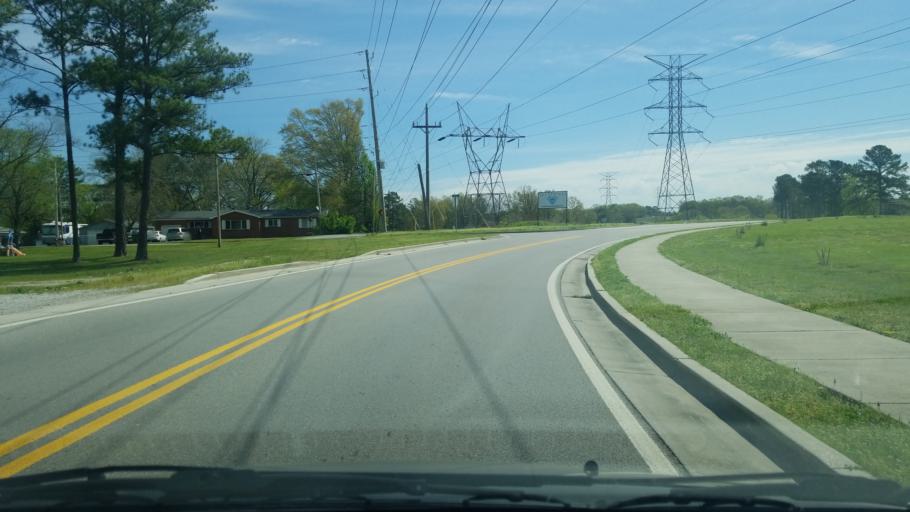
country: US
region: Georgia
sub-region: Catoosa County
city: Fort Oglethorpe
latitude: 34.9568
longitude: -85.2477
